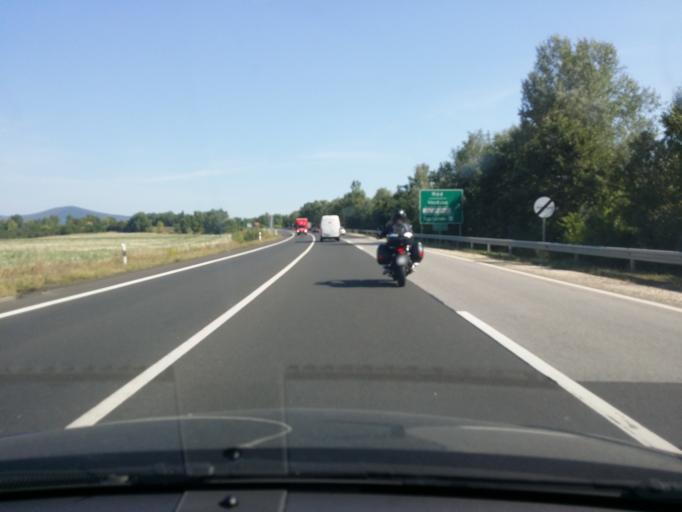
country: HU
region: Pest
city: Szod
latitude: 47.7628
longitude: 19.1815
